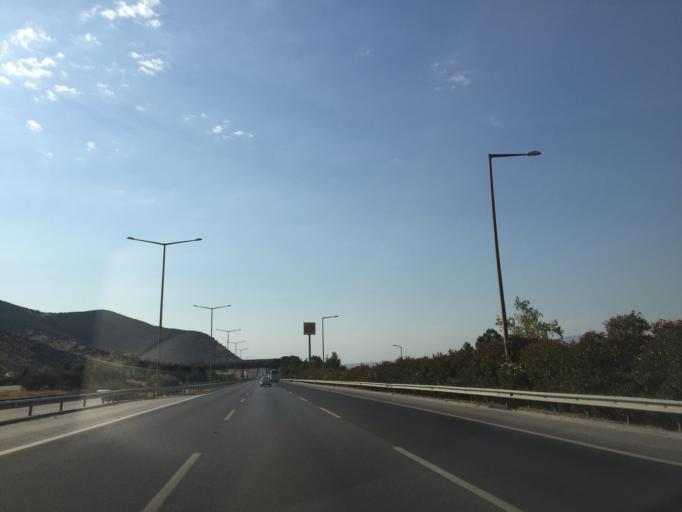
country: TR
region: Izmir
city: Belevi
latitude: 38.0678
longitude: 27.4137
